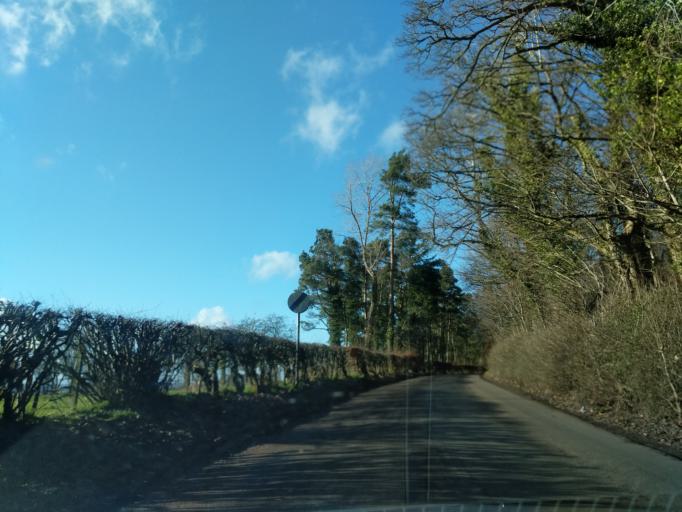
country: GB
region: Scotland
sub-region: South Lanarkshire
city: Carluke
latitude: 55.7093
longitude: -3.8463
